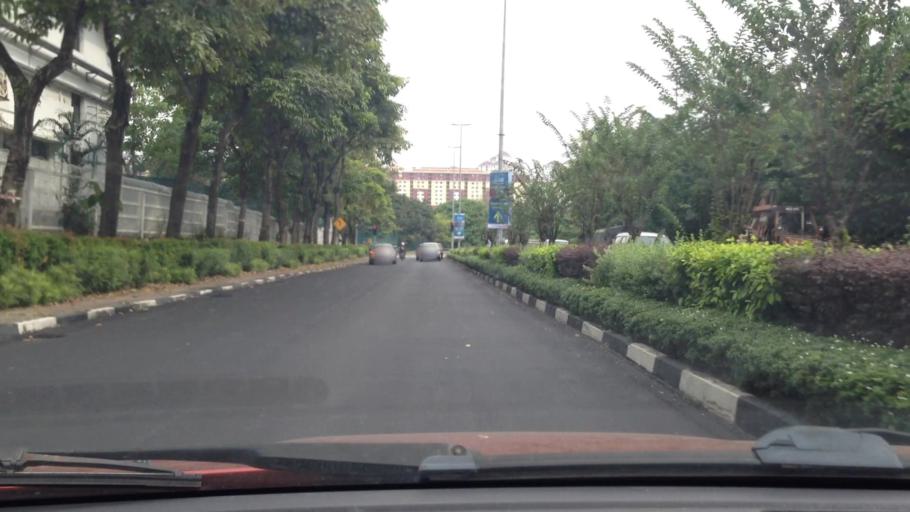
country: MY
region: Selangor
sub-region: Petaling
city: Petaling Jaya
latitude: 3.0888
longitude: 101.6071
